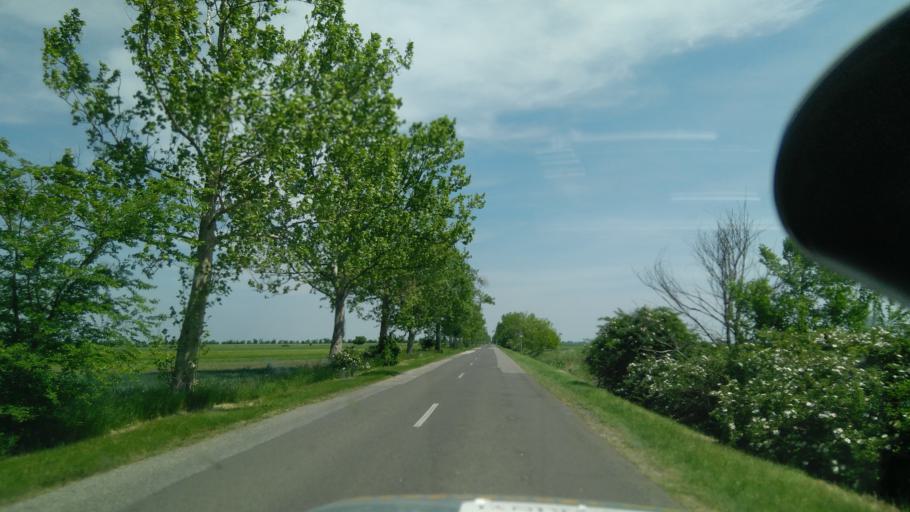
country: HU
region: Csongrad
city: Szekkutas
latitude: 46.5779
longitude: 20.5011
